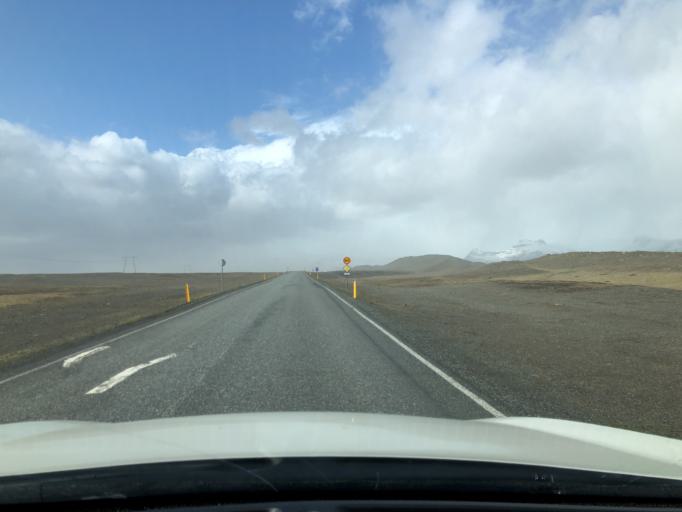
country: IS
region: East
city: Hoefn
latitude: 64.0447
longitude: -16.1857
